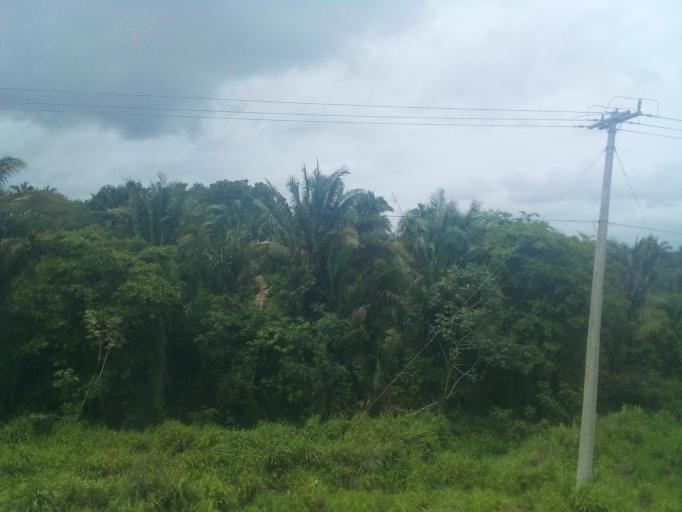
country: BR
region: Maranhao
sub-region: Vitoria Do Mearim
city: Vitoria do Mearim
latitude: -3.5496
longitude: -44.8277
